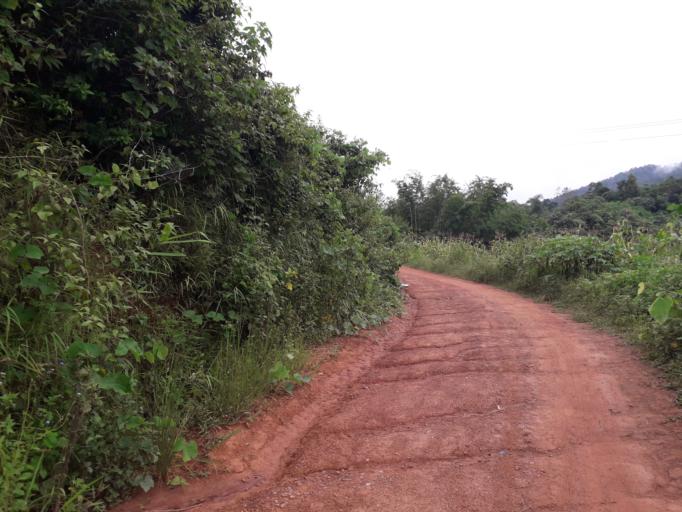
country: CN
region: Yunnan
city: Menglie
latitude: 22.2411
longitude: 101.6131
